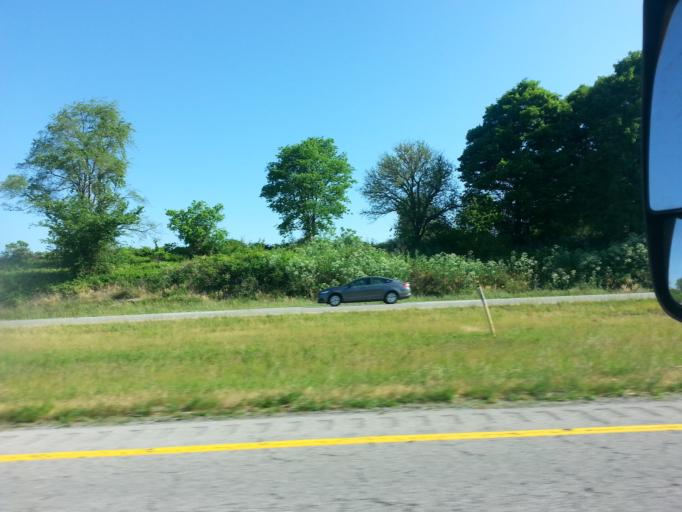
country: US
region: Kentucky
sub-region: Shelby County
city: Shelbyville
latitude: 38.1851
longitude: -85.2401
